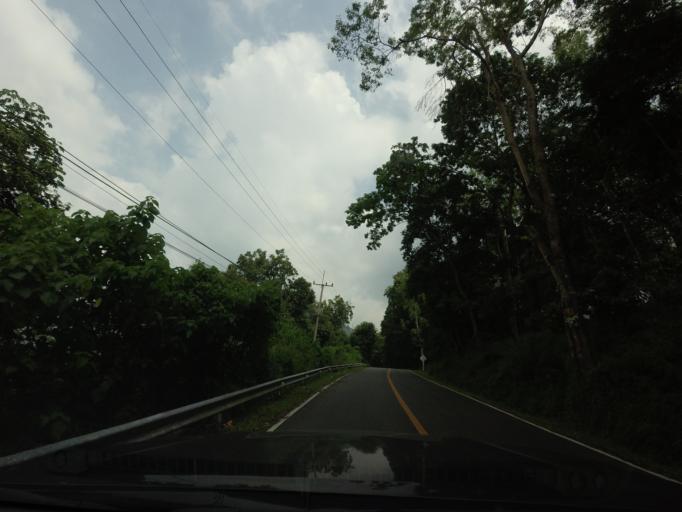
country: TH
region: Nan
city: Pua
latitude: 19.1848
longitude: 101.0069
